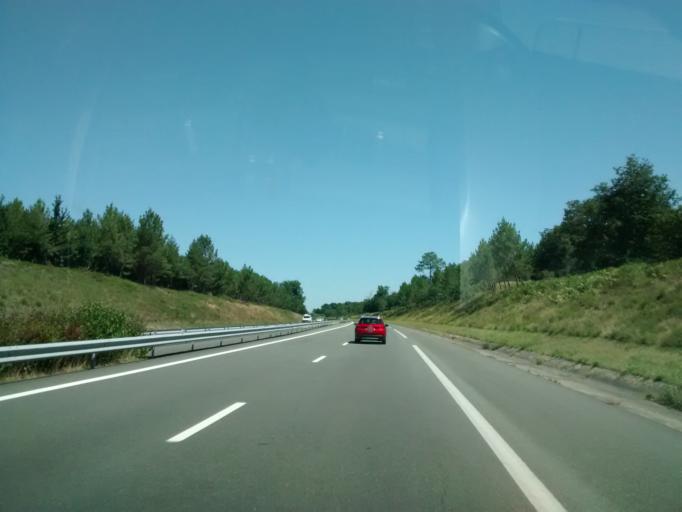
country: FR
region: Aquitaine
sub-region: Departement de la Dordogne
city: Le Pizou
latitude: 44.9858
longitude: 0.0740
